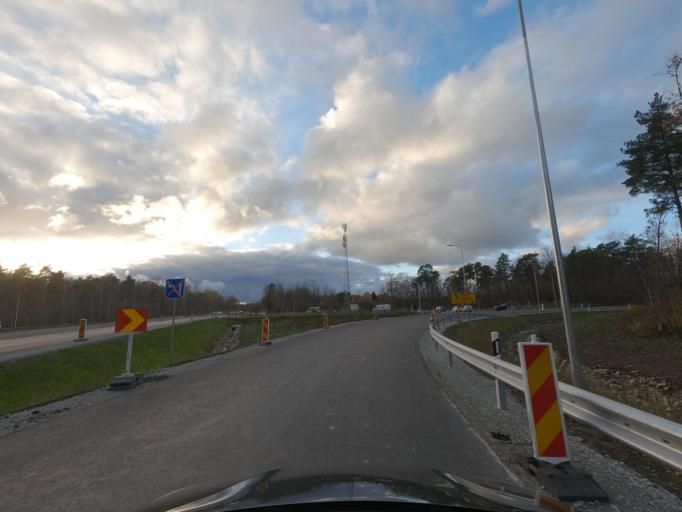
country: EE
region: Harju
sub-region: Saue linn
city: Saue
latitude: 59.3174
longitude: 24.5084
